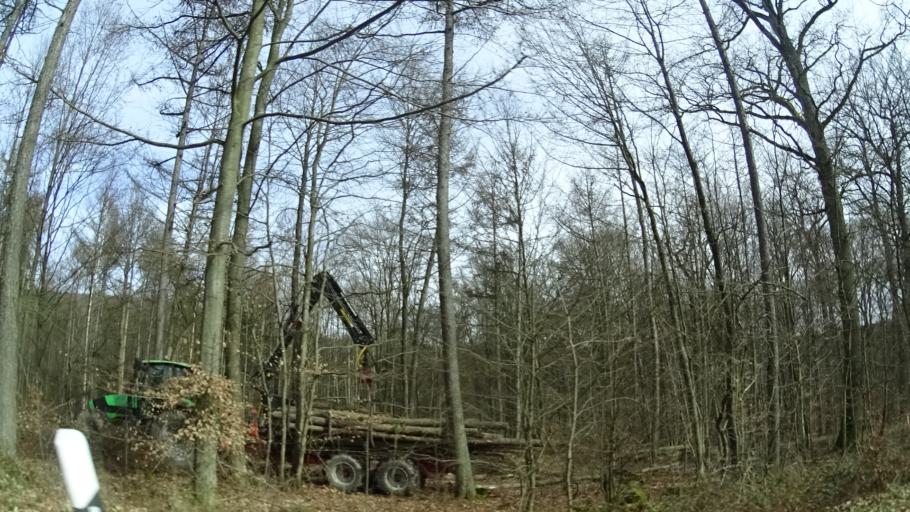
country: DE
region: Rheinland-Pfalz
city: Munchwald
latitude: 49.9025
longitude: 7.6776
